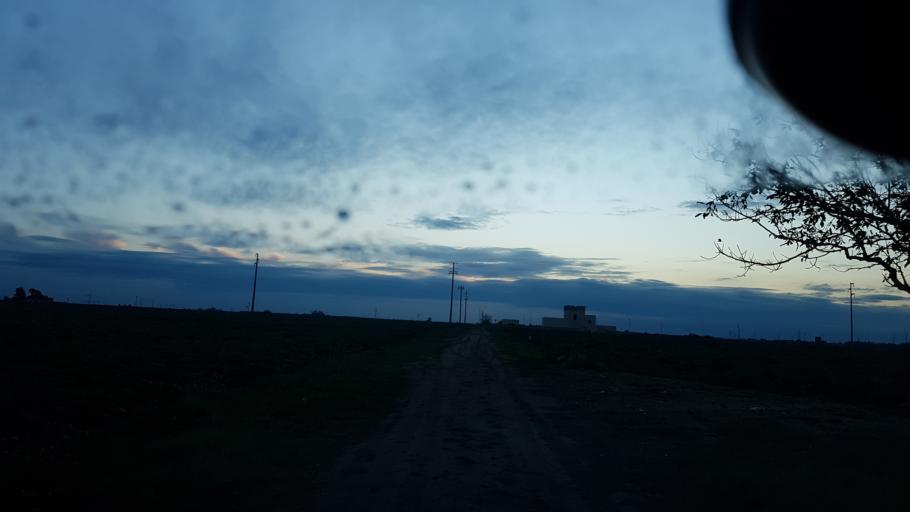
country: IT
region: Apulia
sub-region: Provincia di Brindisi
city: La Rosa
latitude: 40.6060
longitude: 18.0075
